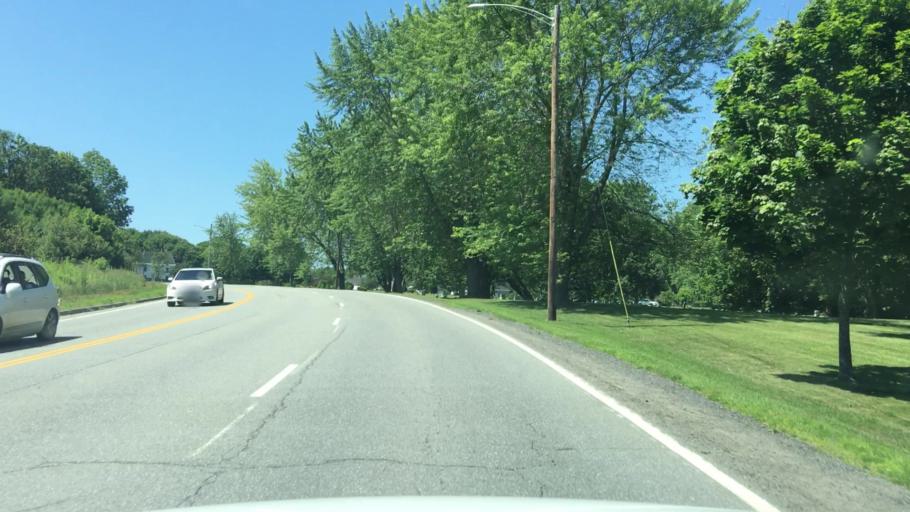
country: US
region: Maine
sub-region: Penobscot County
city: Bangor
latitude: 44.8122
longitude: -68.7855
